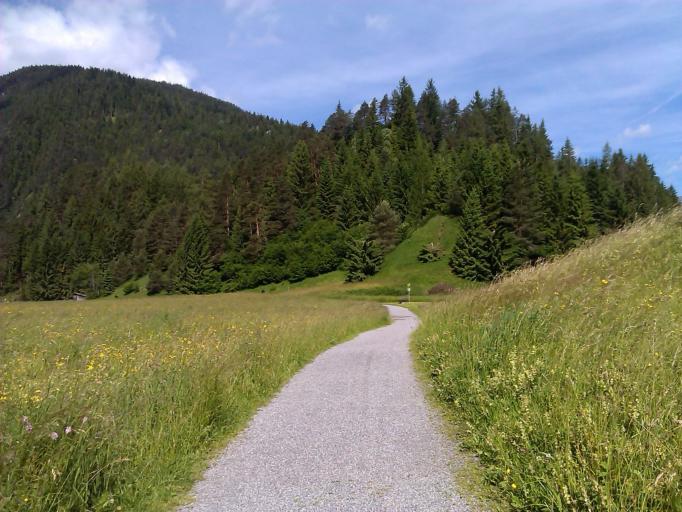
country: AT
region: Tyrol
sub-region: Politischer Bezirk Reutte
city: Biberwier
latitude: 47.3822
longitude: 10.8996
